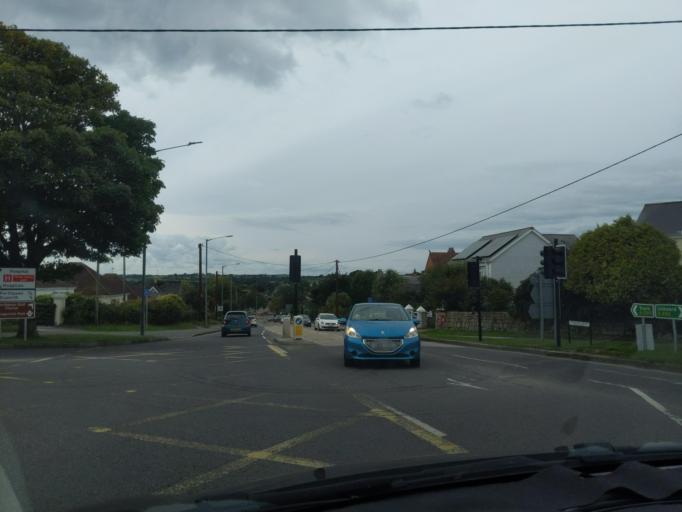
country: GB
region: England
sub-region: Cornwall
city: St Austell
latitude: 50.3365
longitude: -4.7721
